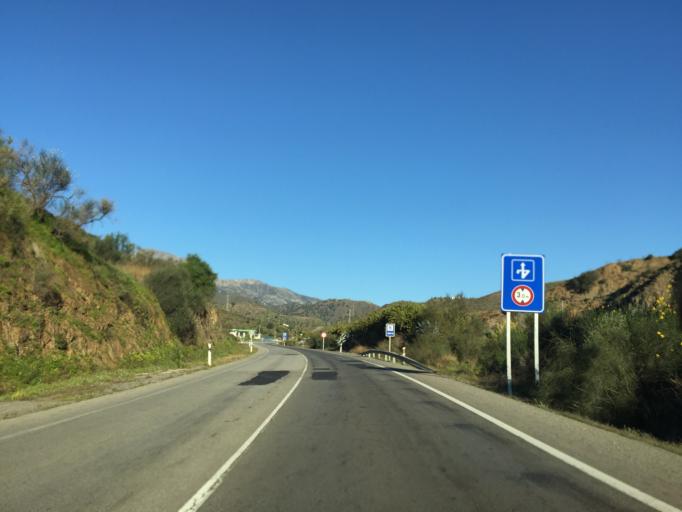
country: ES
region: Andalusia
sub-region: Provincia de Malaga
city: Carratraca
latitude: 36.8088
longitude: -4.7786
